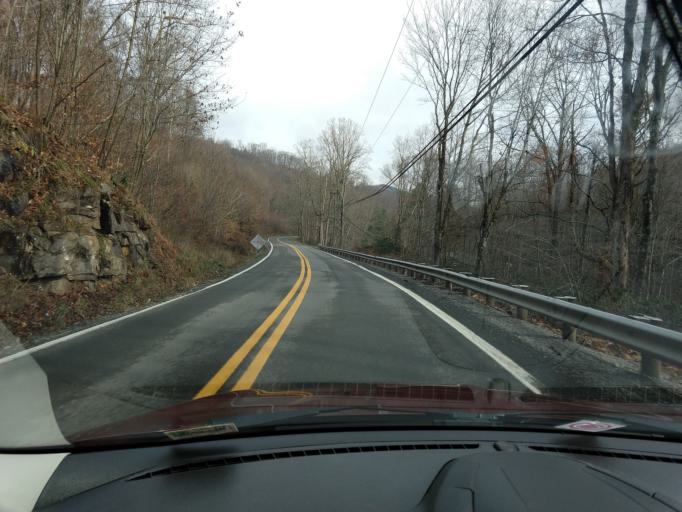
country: US
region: West Virginia
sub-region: Greenbrier County
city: Rainelle
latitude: 38.0896
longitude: -80.7062
